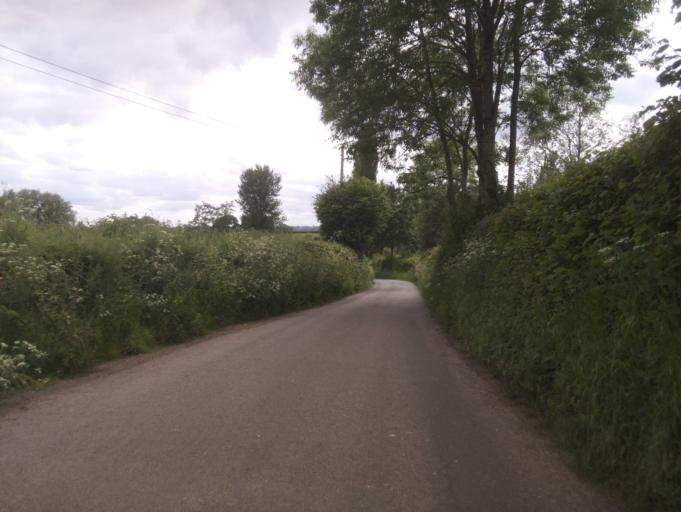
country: GB
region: England
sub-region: Herefordshire
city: Ledbury
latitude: 52.0329
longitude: -2.4703
